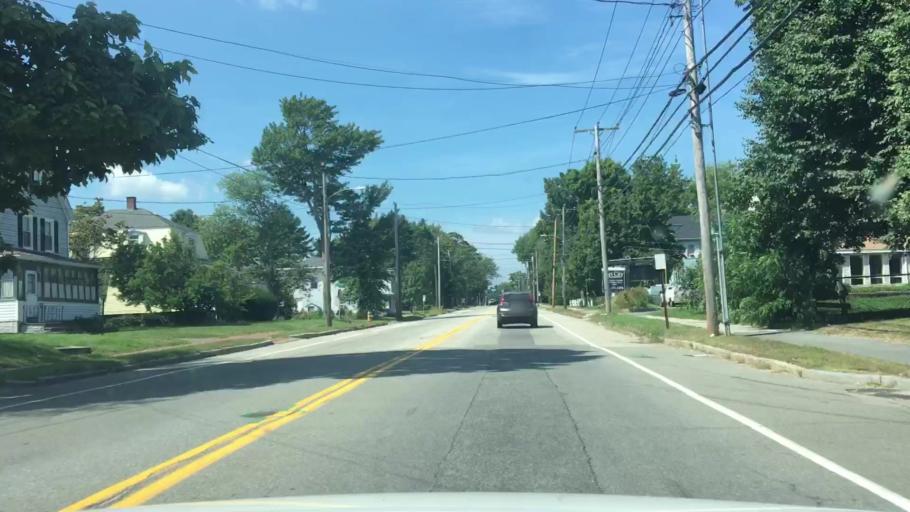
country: US
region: Maine
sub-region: Cumberland County
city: Portland
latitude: 43.6890
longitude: -70.2744
